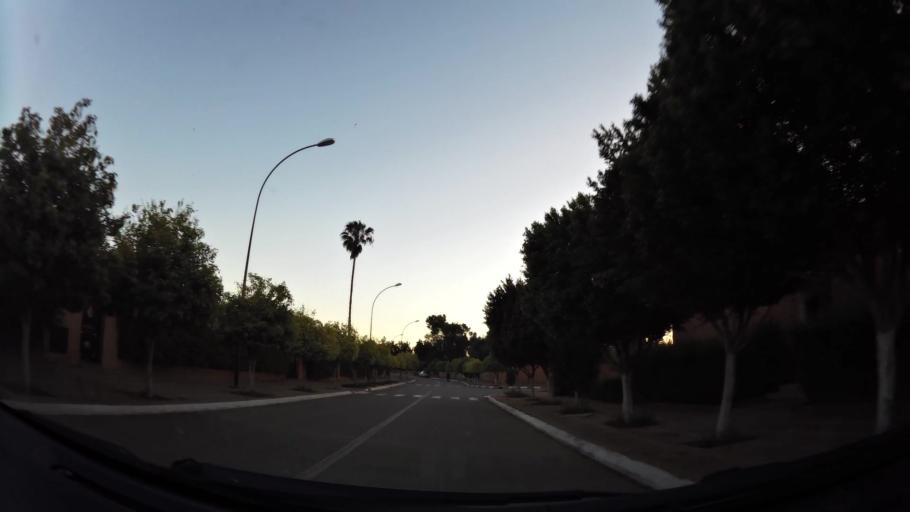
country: MA
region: Marrakech-Tensift-Al Haouz
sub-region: Kelaa-Des-Sraghna
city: Sidi Bou Othmane
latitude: 32.2127
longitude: -7.9303
